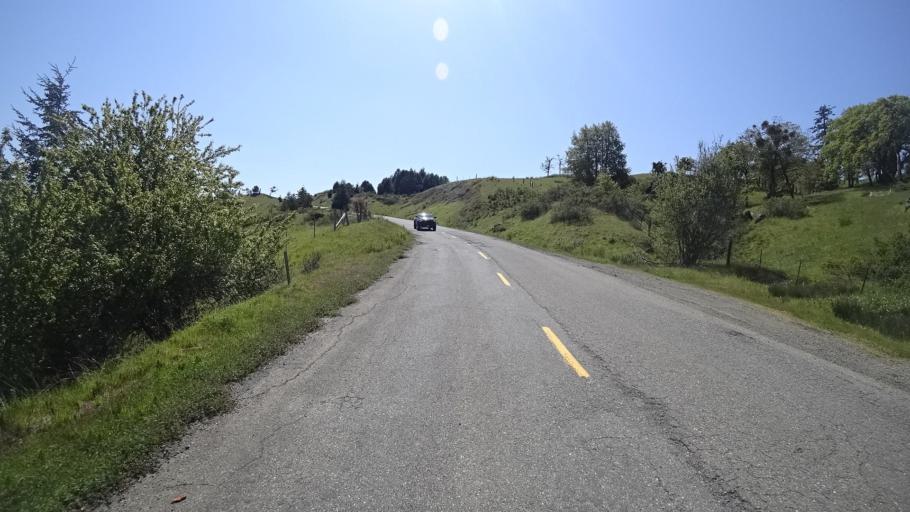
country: US
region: California
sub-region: Humboldt County
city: Redway
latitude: 40.1112
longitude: -123.6722
